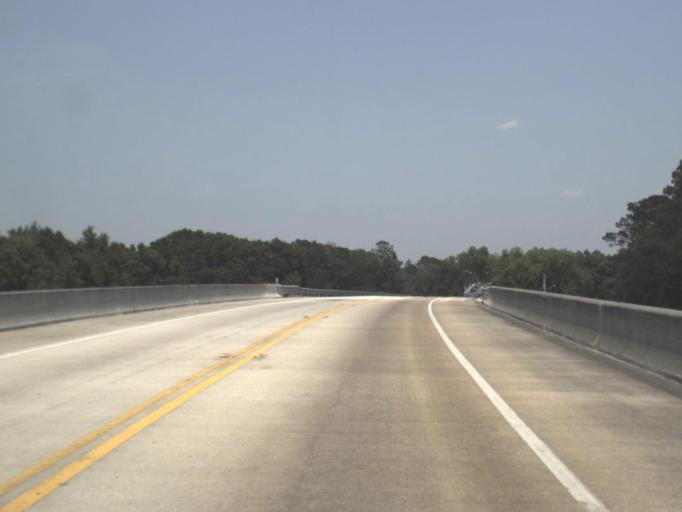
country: US
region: Florida
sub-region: Duval County
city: Baldwin
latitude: 30.2013
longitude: -82.0132
